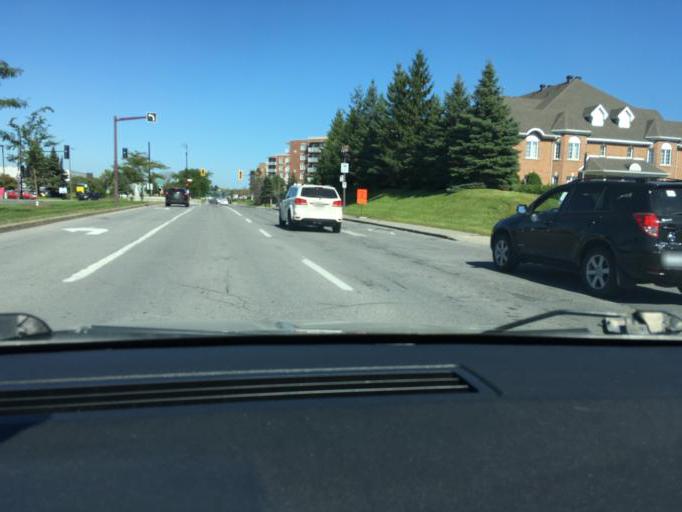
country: CA
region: Quebec
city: Dorval
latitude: 45.5089
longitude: -73.7357
